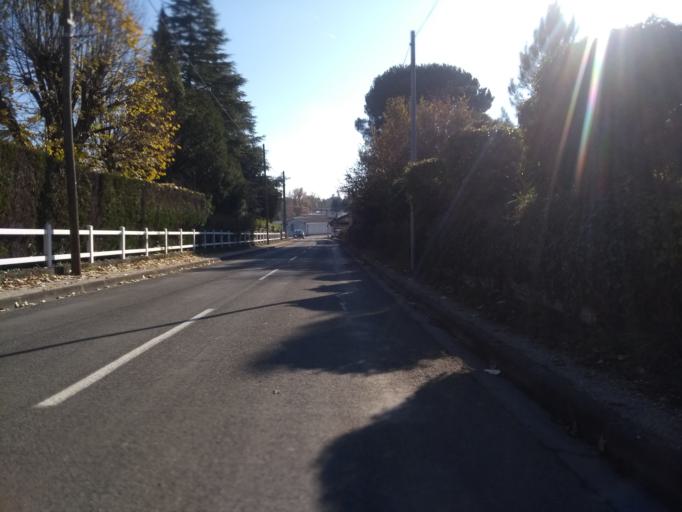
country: FR
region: Aquitaine
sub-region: Departement de la Gironde
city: Leognan
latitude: 44.7338
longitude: -0.6002
